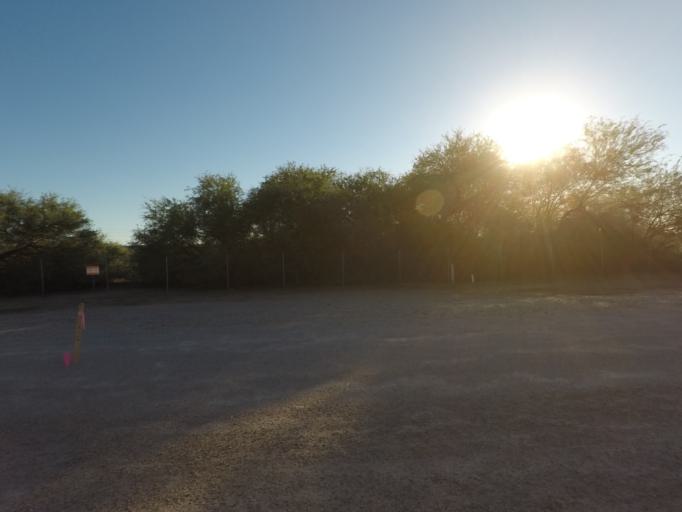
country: US
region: Arizona
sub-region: Maricopa County
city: Tempe Junction
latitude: 33.4452
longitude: -111.9851
